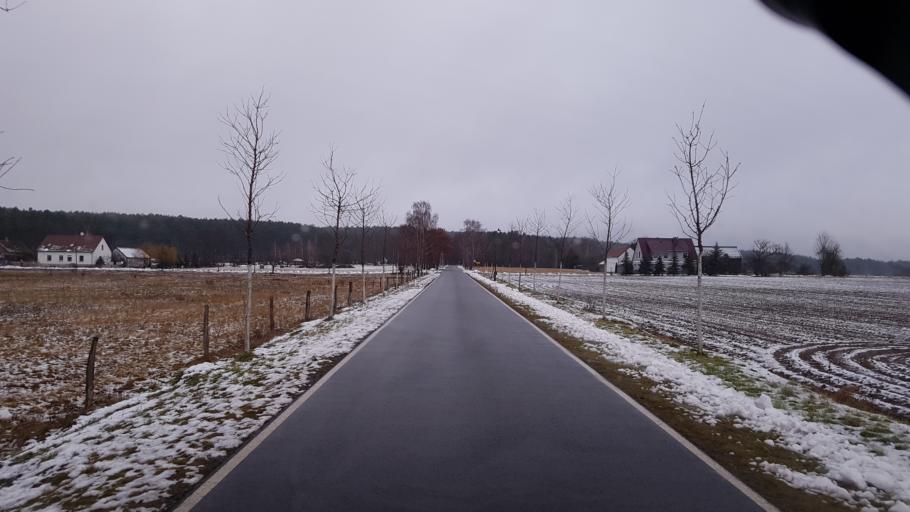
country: DE
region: Brandenburg
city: Neu Zauche
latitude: 51.9468
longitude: 14.1160
